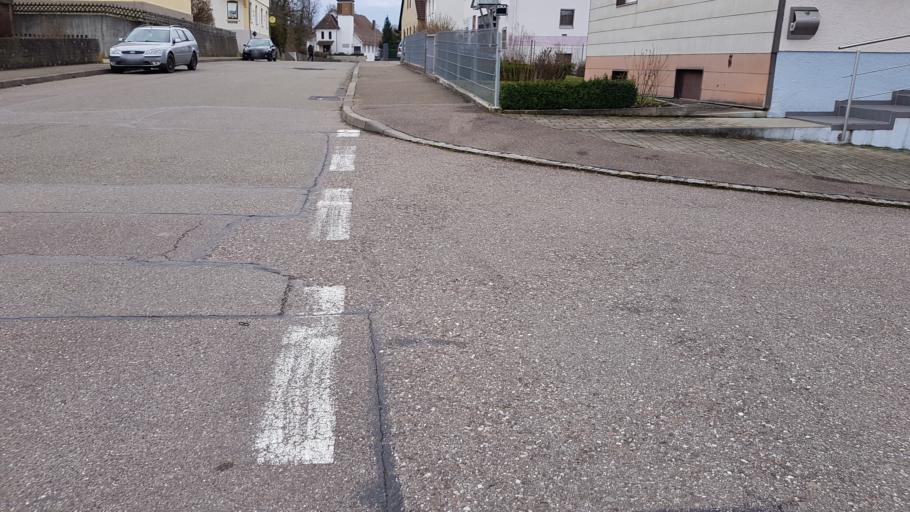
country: DE
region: Baden-Wuerttemberg
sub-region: Regierungsbezirk Stuttgart
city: Giengen an der Brenz
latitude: 48.6269
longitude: 10.2433
